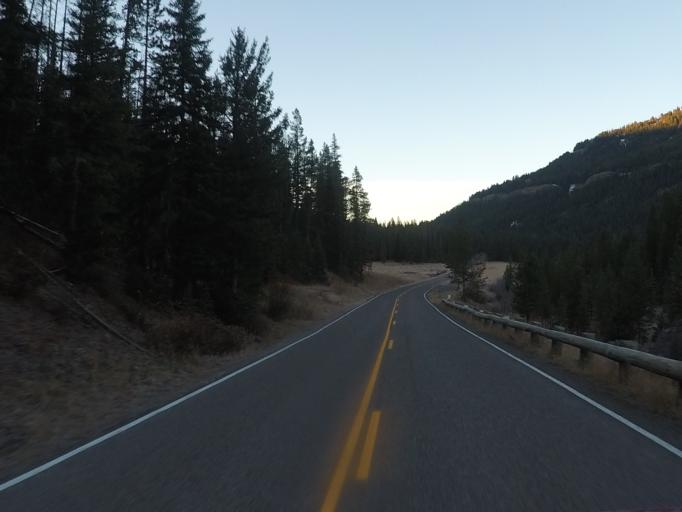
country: US
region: Montana
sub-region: Stillwater County
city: Absarokee
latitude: 44.9532
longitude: -110.0749
